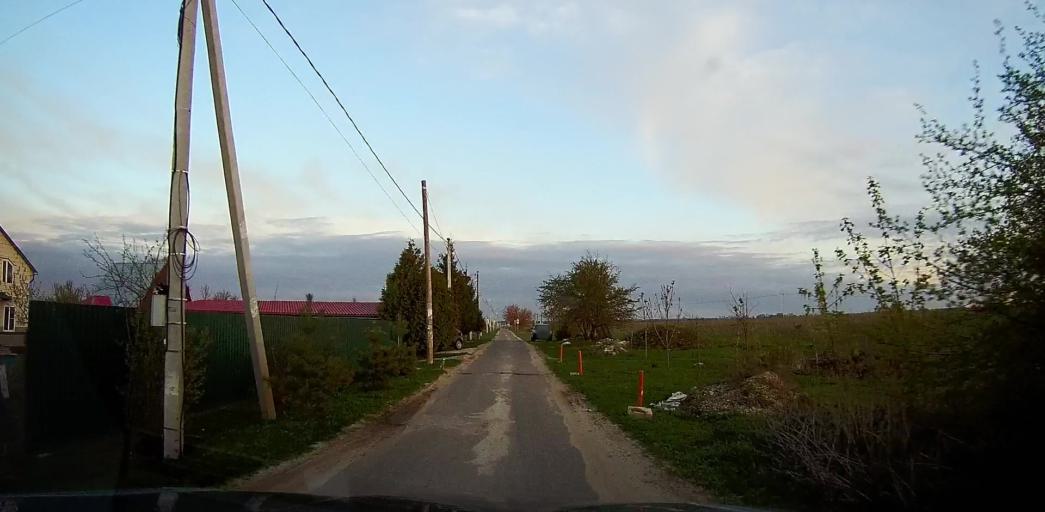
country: RU
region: Moskovskaya
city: Peski
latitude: 55.2311
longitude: 38.7328
